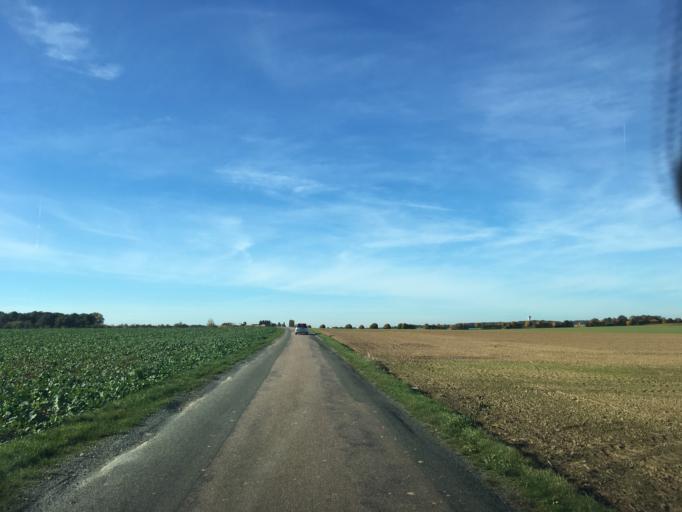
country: FR
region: Haute-Normandie
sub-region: Departement de l'Eure
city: Pacy-sur-Eure
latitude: 49.0416
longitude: 1.4165
